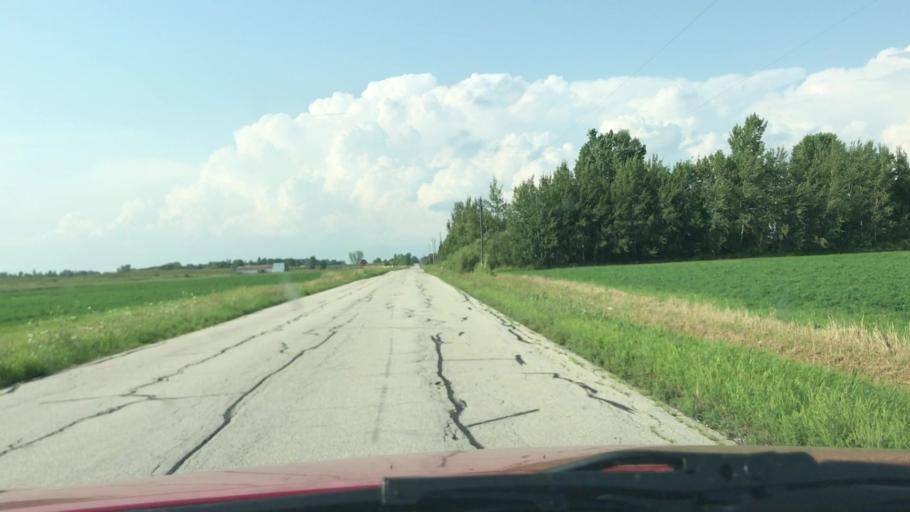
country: US
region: Wisconsin
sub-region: Brown County
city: Oneida
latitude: 44.4323
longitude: -88.1705
